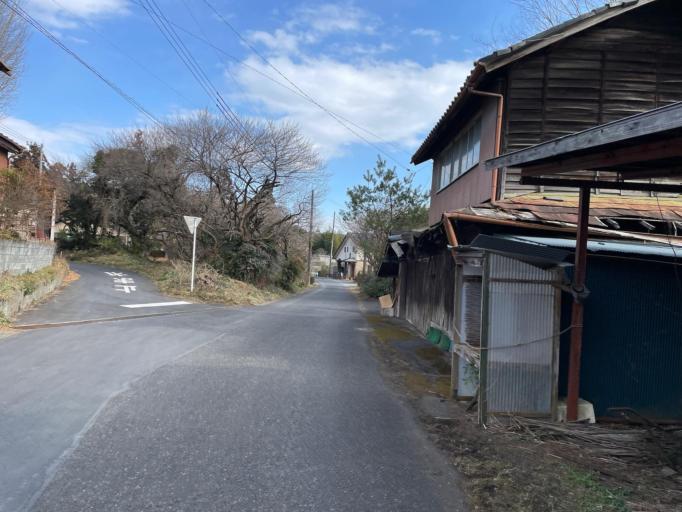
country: JP
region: Saitama
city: Hanno
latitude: 35.8380
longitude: 139.2889
